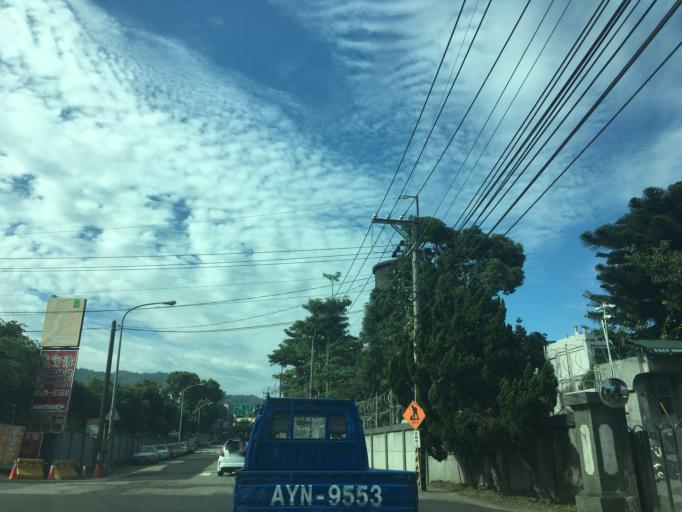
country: TW
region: Taiwan
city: Fengyuan
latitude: 24.2073
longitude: 120.7945
